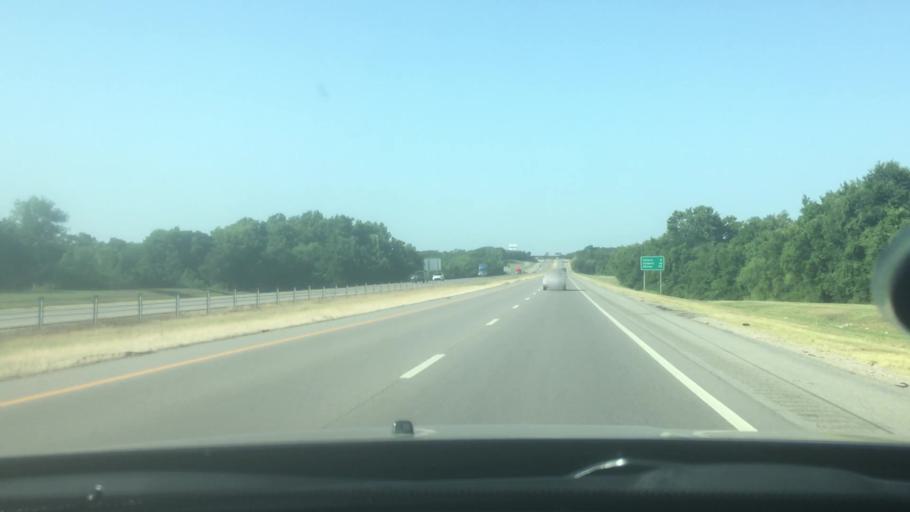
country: US
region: Oklahoma
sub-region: Bryan County
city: Durant
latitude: 33.9923
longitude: -96.4082
